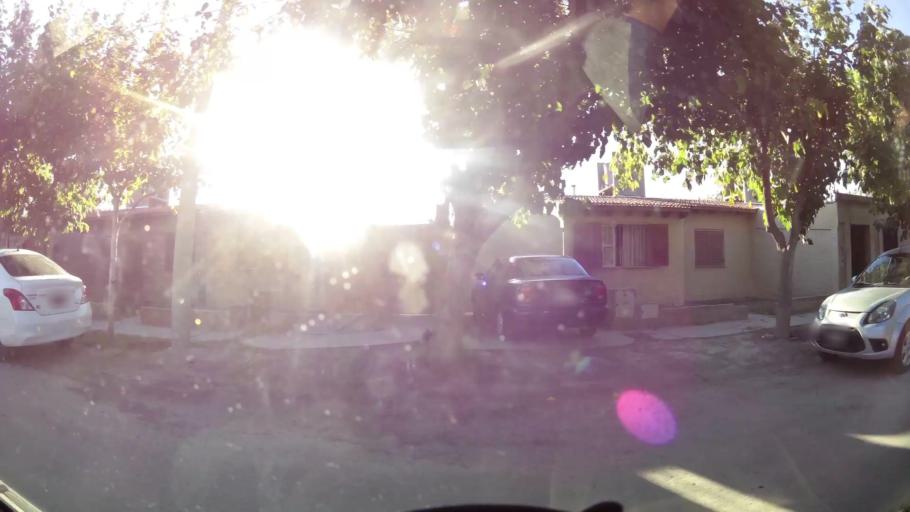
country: AR
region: San Juan
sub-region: Departamento de Santa Lucia
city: Santa Lucia
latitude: -31.5502
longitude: -68.5091
